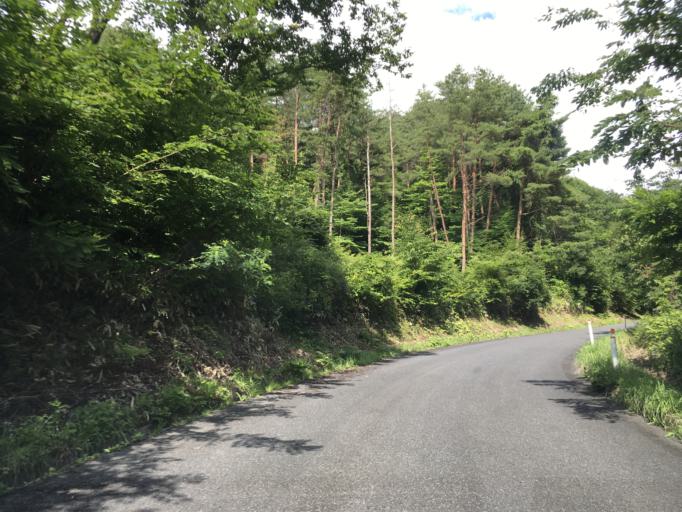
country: JP
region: Iwate
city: Ichinoseki
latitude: 38.9777
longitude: 141.4278
